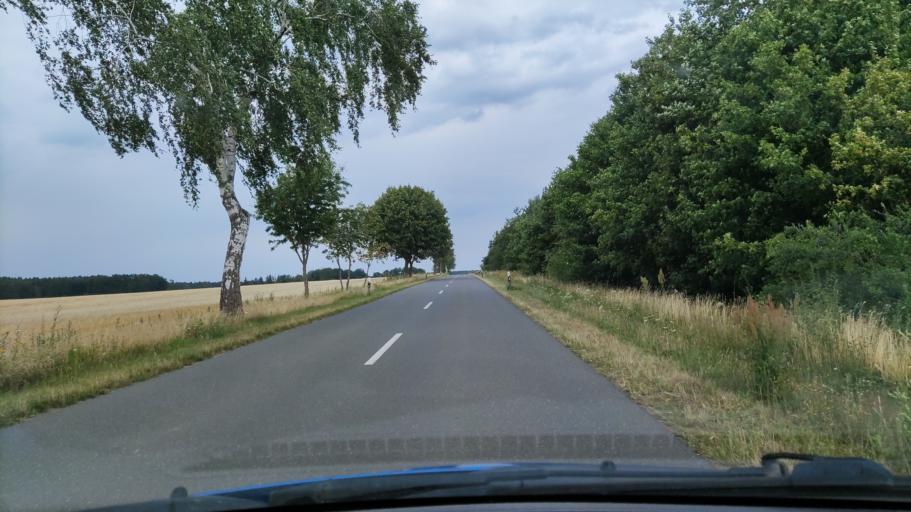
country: DE
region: Lower Saxony
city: Suhlendorf
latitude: 52.9584
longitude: 10.8261
